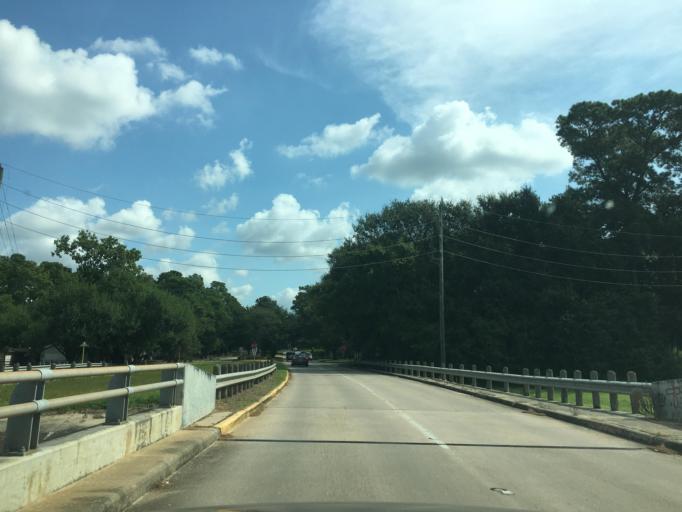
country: US
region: Texas
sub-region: Harris County
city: Spring
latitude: 30.0445
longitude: -95.4463
